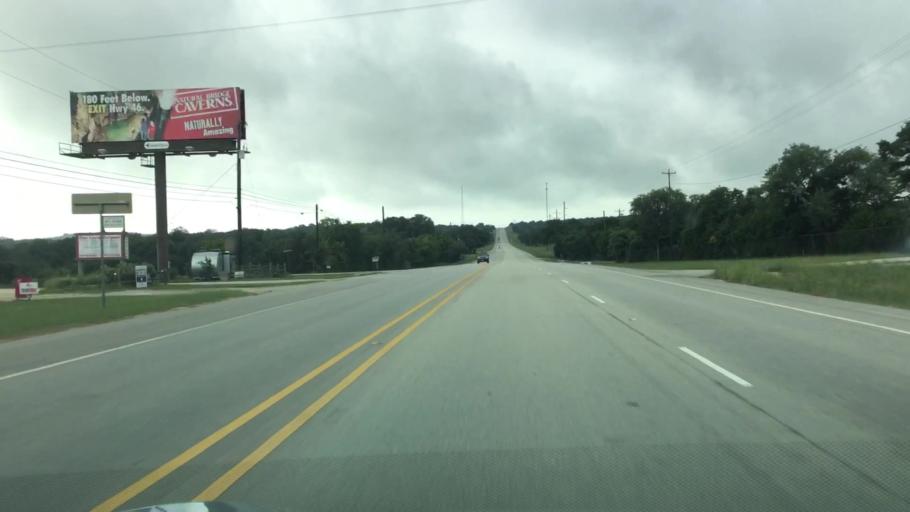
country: US
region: Texas
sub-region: Blanco County
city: Blanco
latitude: 30.0645
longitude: -98.4111
